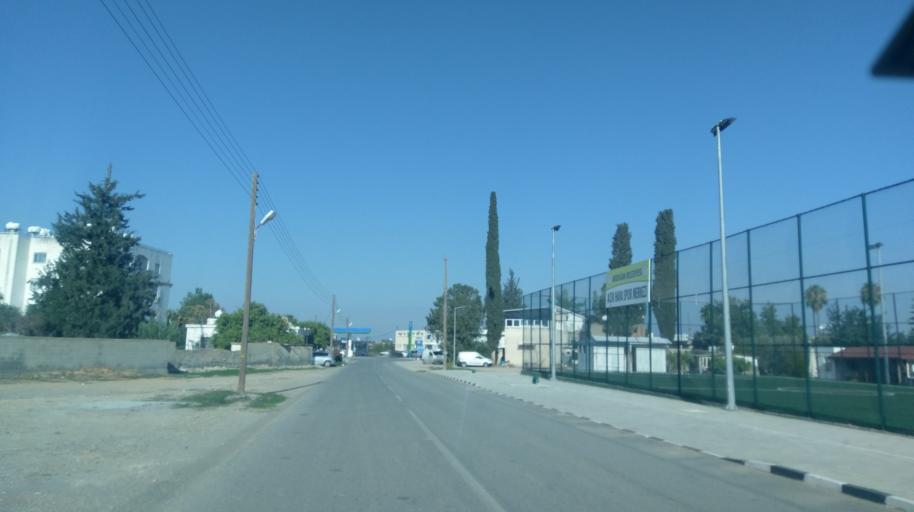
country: CY
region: Larnaka
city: Pergamos
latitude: 35.1091
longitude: 33.6781
